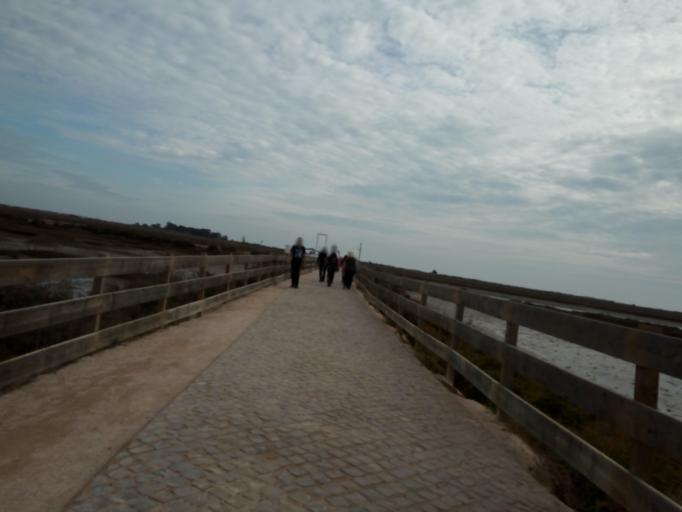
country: PT
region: Faro
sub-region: Tavira
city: Luz
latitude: 37.0928
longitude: -7.6749
